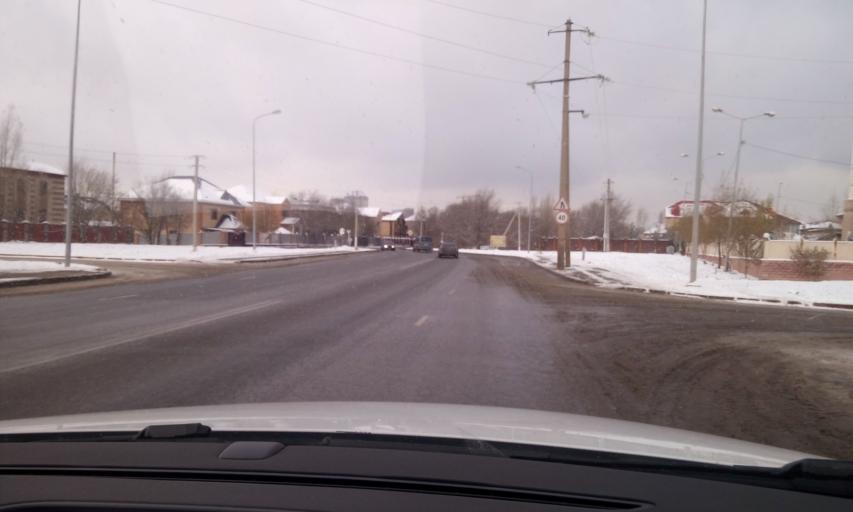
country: KZ
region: Astana Qalasy
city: Astana
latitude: 51.1384
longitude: 71.4346
